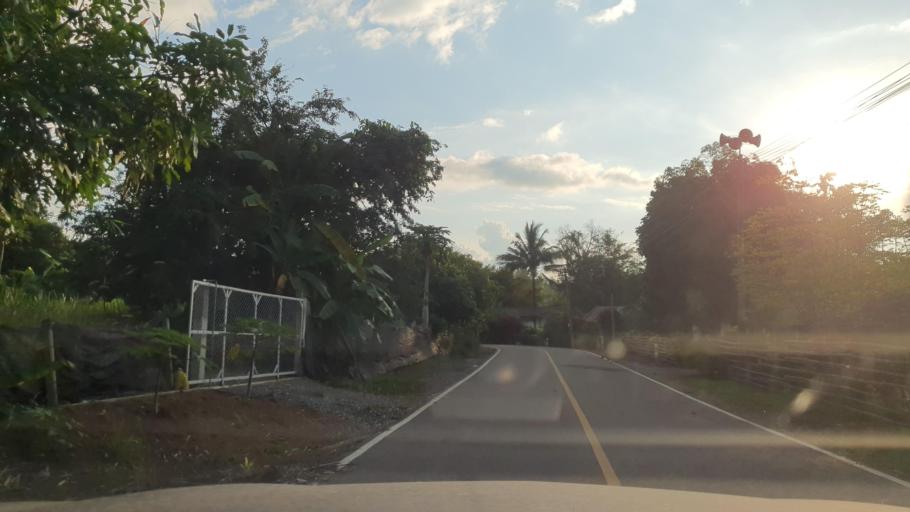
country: TH
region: Chiang Mai
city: Mae On
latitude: 18.8690
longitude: 99.2406
